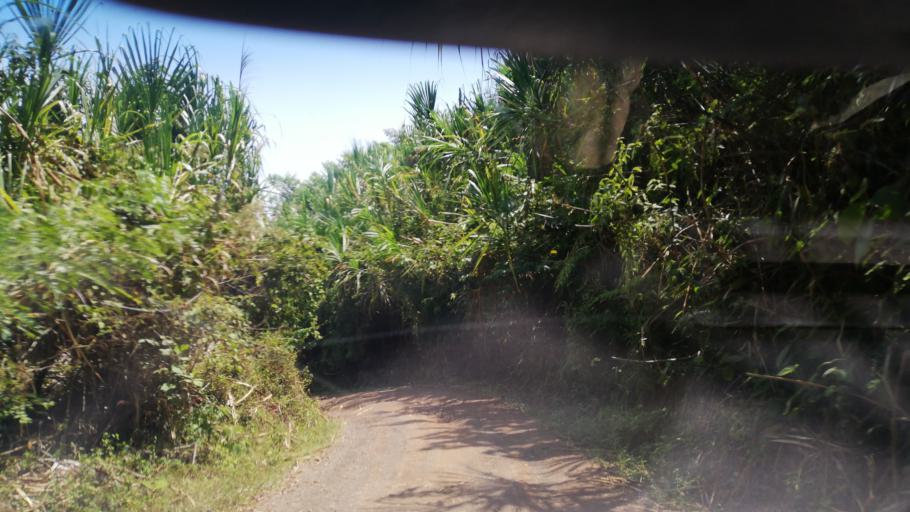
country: CO
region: Risaralda
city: La Virginia
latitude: 4.8778
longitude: -75.9449
